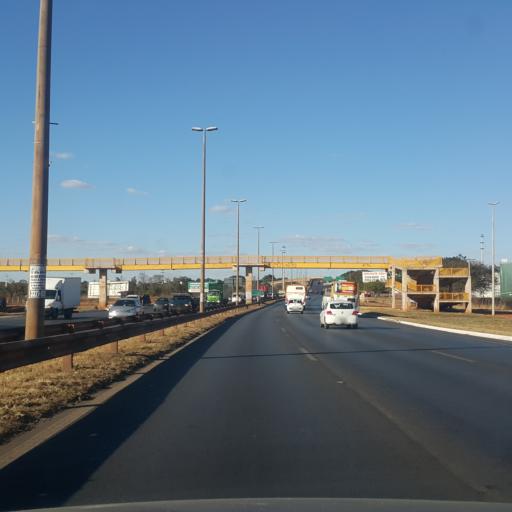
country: BR
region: Federal District
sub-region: Brasilia
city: Brasilia
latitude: -15.7875
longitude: -47.9465
